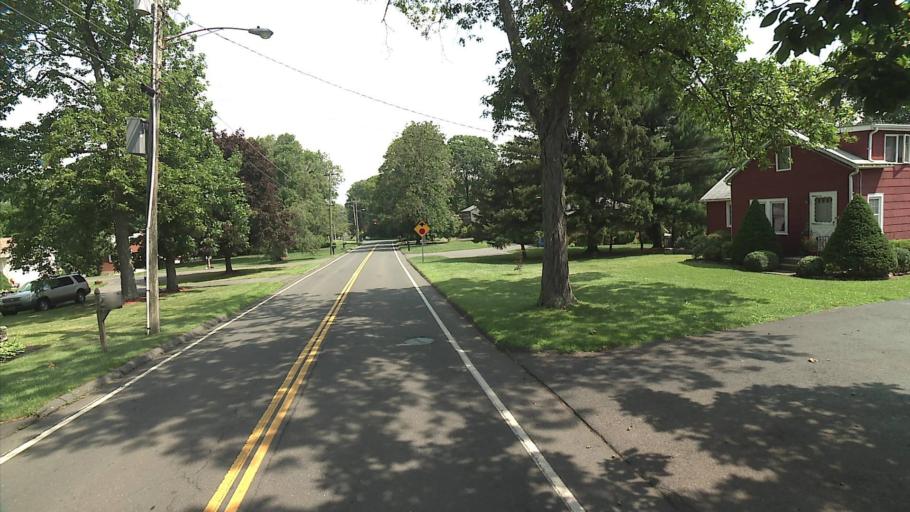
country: US
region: Connecticut
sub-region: Middlesex County
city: Middletown
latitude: 41.5622
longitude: -72.7017
